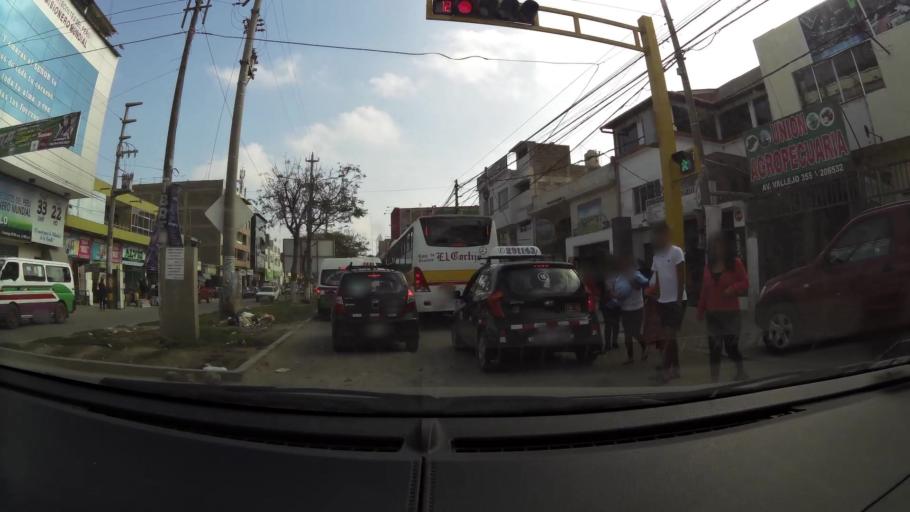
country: PE
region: La Libertad
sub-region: Provincia de Trujillo
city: Trujillo
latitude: -8.1103
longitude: -79.0176
